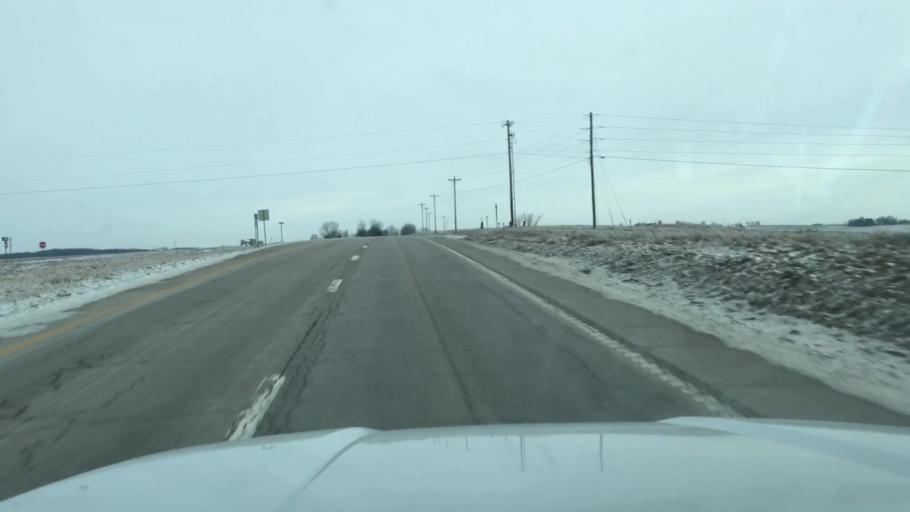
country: US
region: Missouri
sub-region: Andrew County
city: Savannah
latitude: 39.9806
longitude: -94.8783
